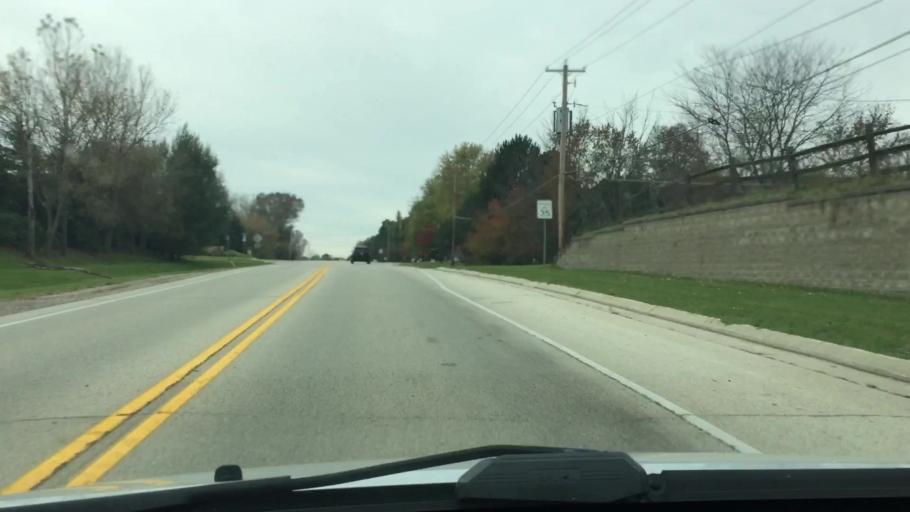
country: US
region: Wisconsin
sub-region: Waukesha County
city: Mukwonago
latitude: 42.8742
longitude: -88.3112
